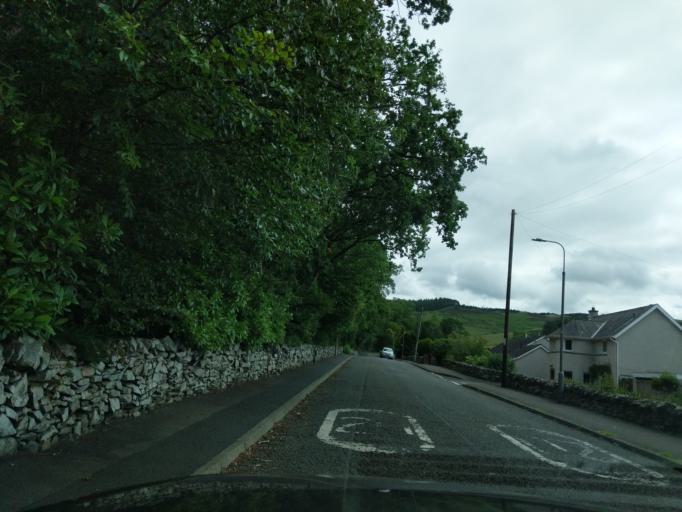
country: GB
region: Scotland
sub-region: The Scottish Borders
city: Peebles
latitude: 55.6459
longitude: -3.1992
